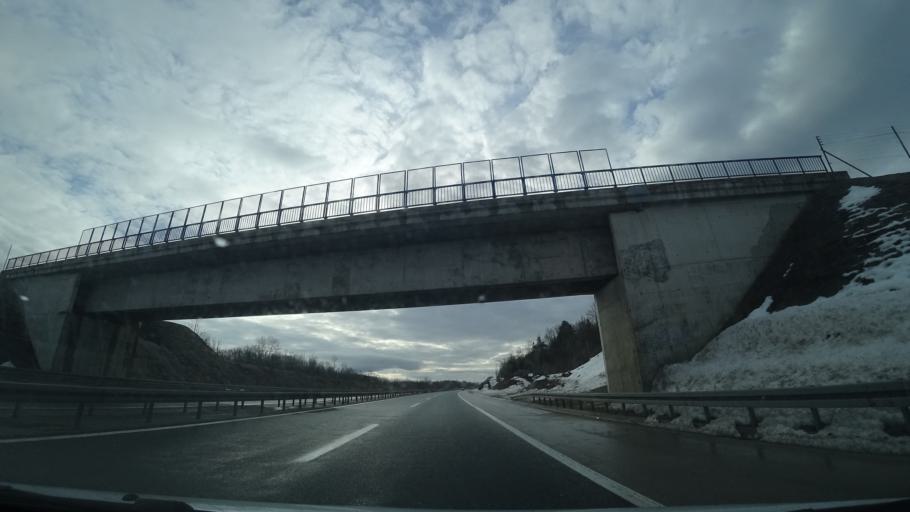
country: HR
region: Licko-Senjska
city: Otocac
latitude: 44.7572
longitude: 15.3663
